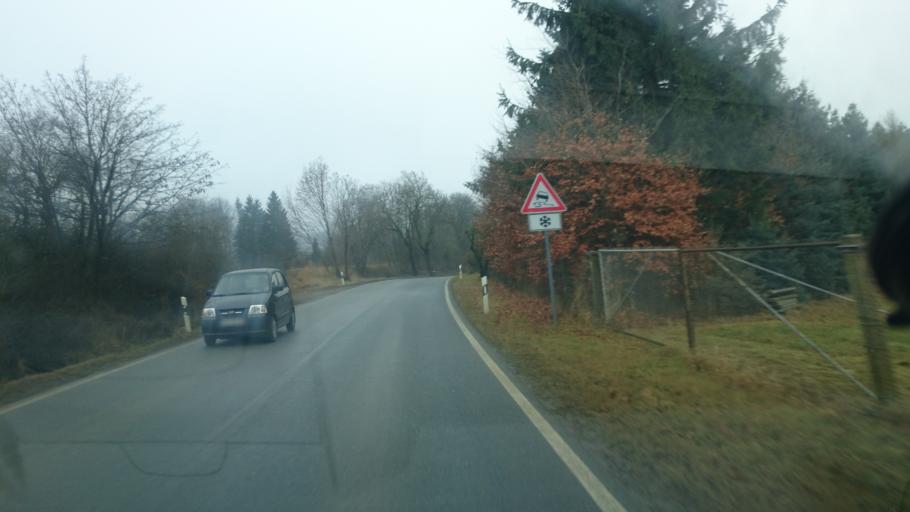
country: DE
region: Thuringia
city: Tanna
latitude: 50.4936
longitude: 11.8501
